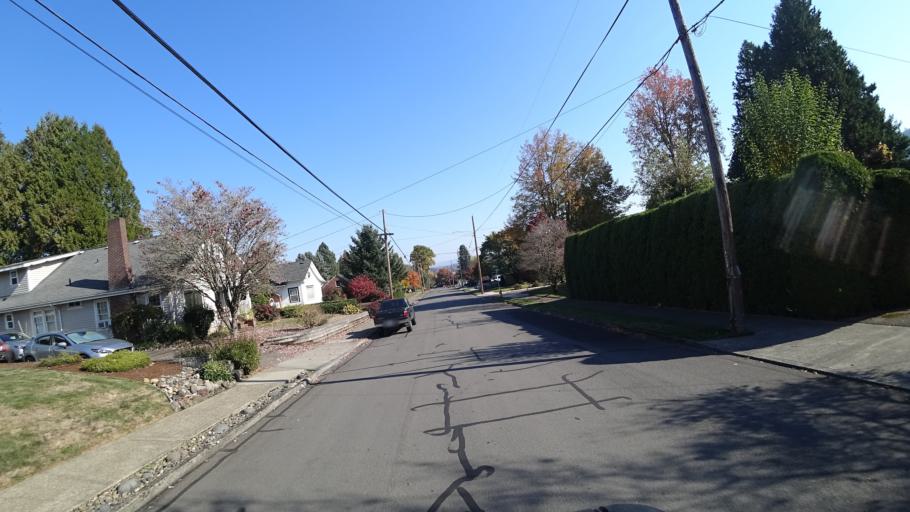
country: US
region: Oregon
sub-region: Multnomah County
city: Gresham
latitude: 45.4988
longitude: -122.4419
